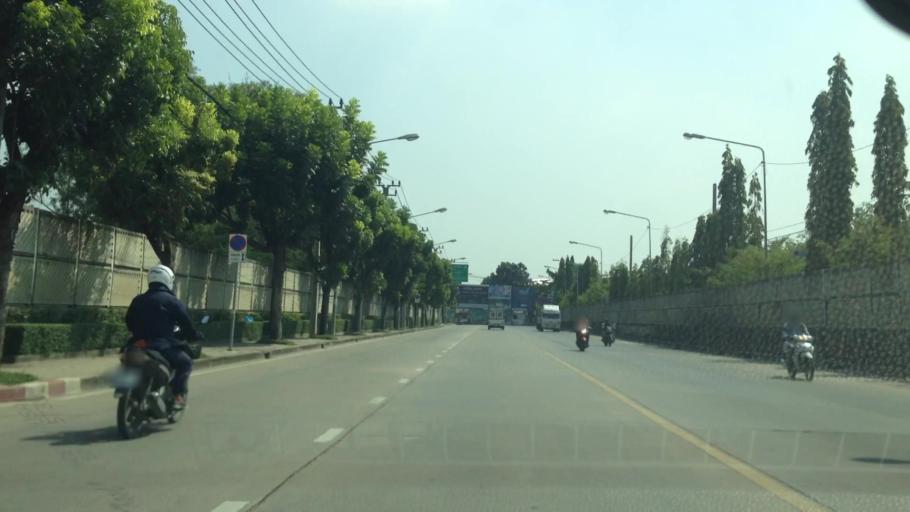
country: TH
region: Bangkok
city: Sai Mai
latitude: 13.9203
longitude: 100.6306
